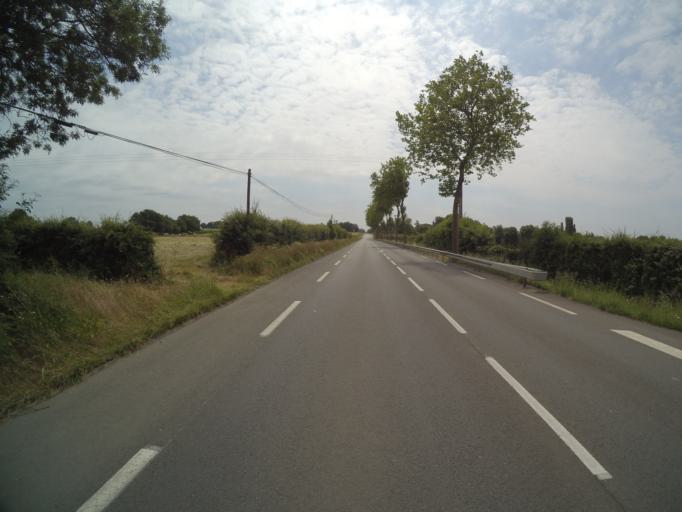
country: FR
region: Pays de la Loire
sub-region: Departement de la Vendee
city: Saint-Fulgent
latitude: 46.8768
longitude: -1.2047
